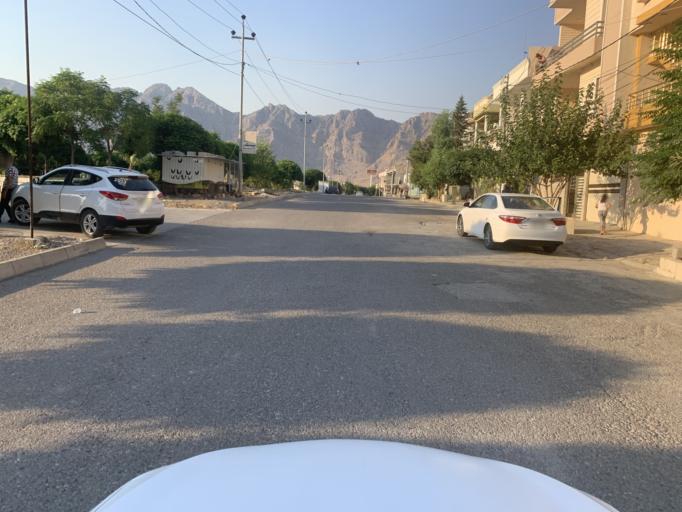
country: IQ
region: As Sulaymaniyah
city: Raniye
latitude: 36.2441
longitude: 44.8805
